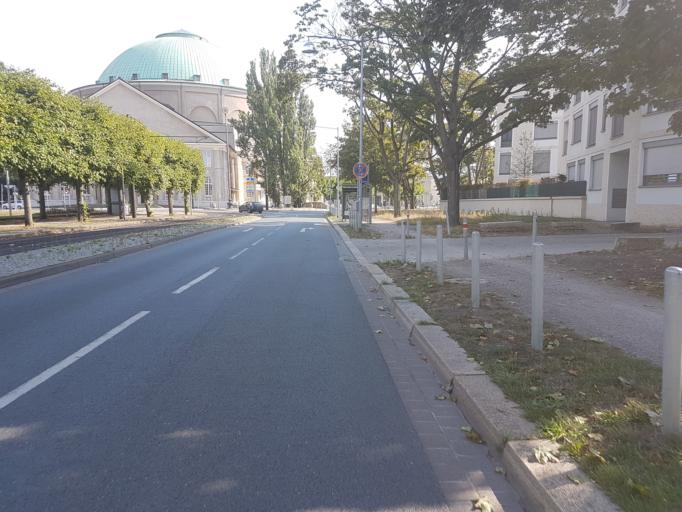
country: DE
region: Lower Saxony
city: Hannover
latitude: 52.3773
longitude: 9.7682
